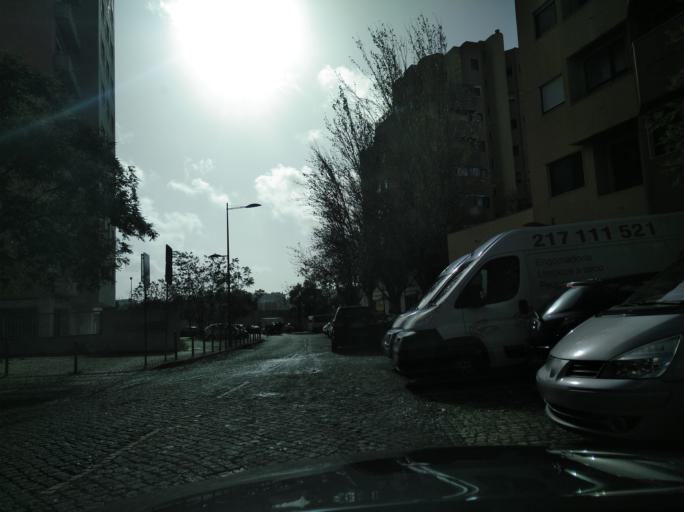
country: PT
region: Lisbon
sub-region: Odivelas
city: Pontinha
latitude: 38.7607
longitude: -9.1784
